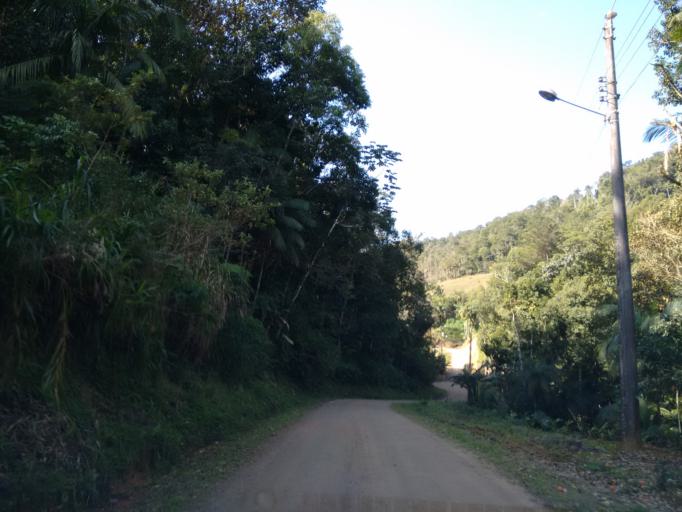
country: BR
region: Santa Catarina
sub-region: Pomerode
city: Pomerode
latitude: -26.7434
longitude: -49.1539
